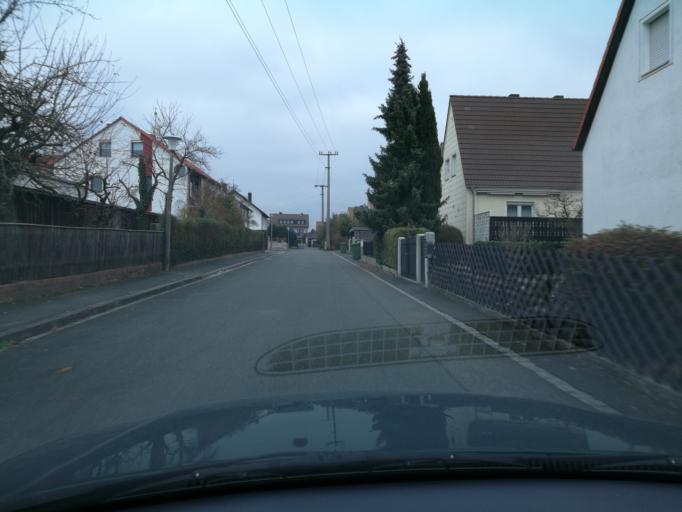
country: DE
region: Bavaria
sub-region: Regierungsbezirk Mittelfranken
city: Seukendorf
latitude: 49.4857
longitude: 10.8849
